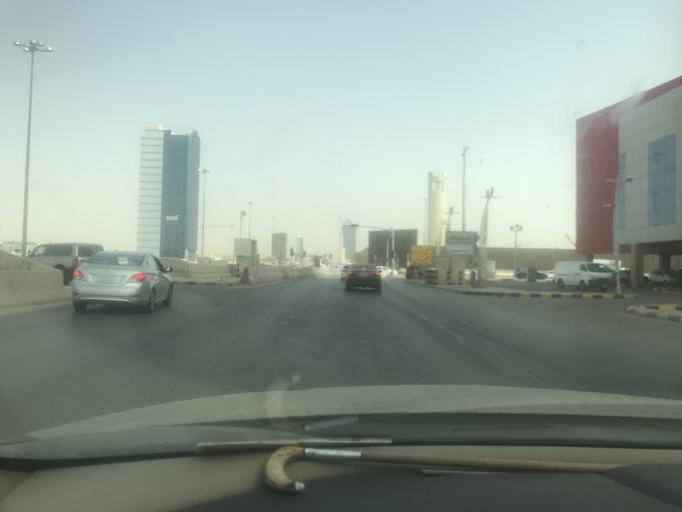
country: SA
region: Ar Riyad
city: Riyadh
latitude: 24.8095
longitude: 46.6231
